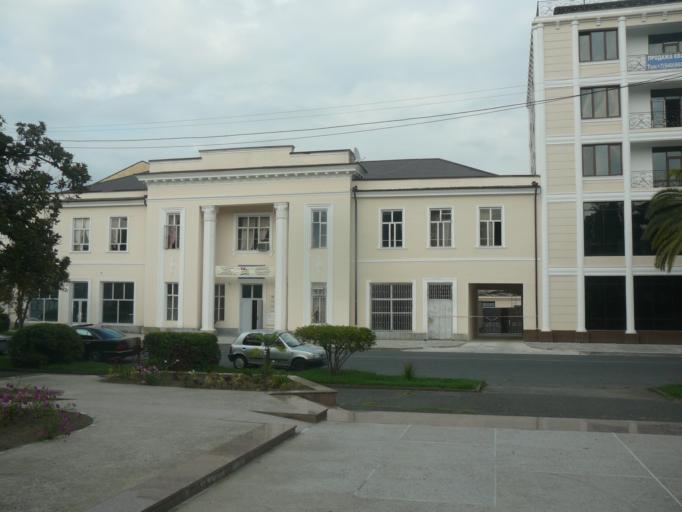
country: GE
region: Abkhazia
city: Sokhumi
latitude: 43.0004
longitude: 41.0216
